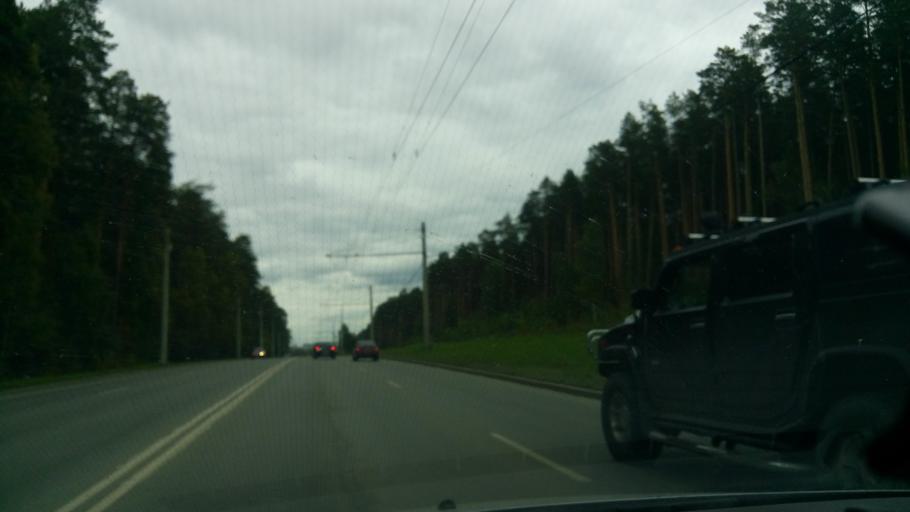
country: RU
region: Sverdlovsk
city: Sovkhoznyy
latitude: 56.7858
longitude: 60.5658
